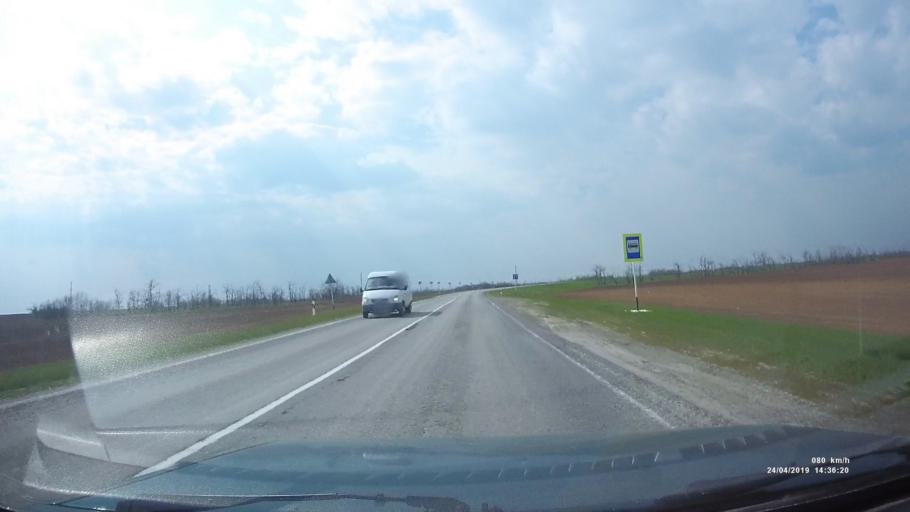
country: RU
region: Rostov
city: Remontnoye
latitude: 46.3751
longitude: 43.8928
